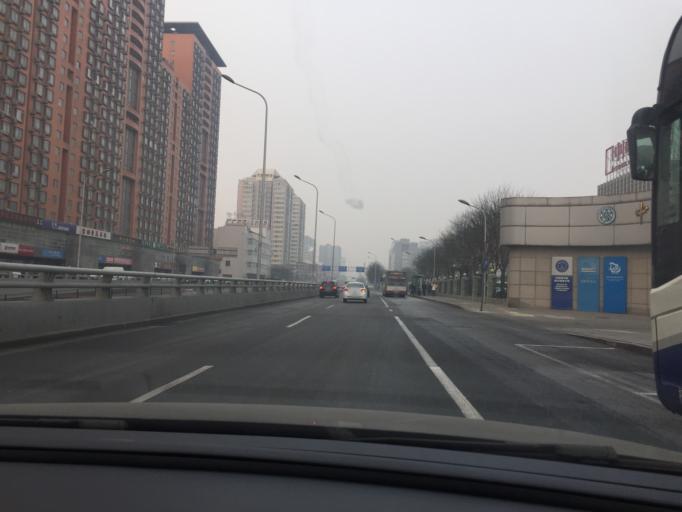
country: CN
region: Beijing
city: Datun
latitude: 40.0007
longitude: 116.3779
